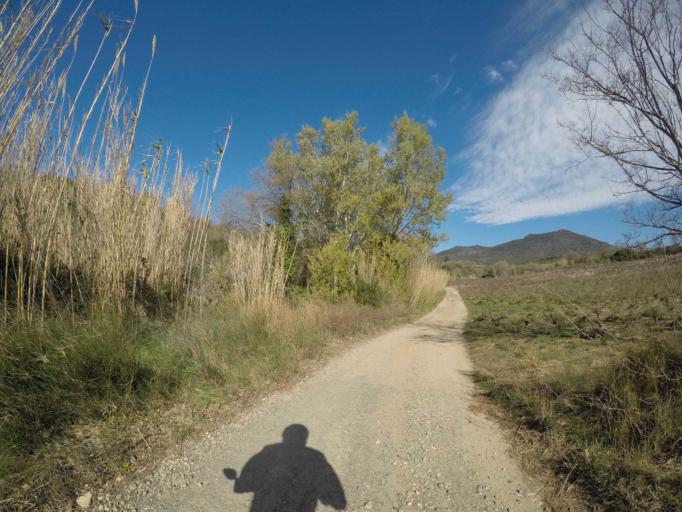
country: FR
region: Languedoc-Roussillon
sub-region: Departement des Pyrenees-Orientales
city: Millas
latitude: 42.7070
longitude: 2.7026
